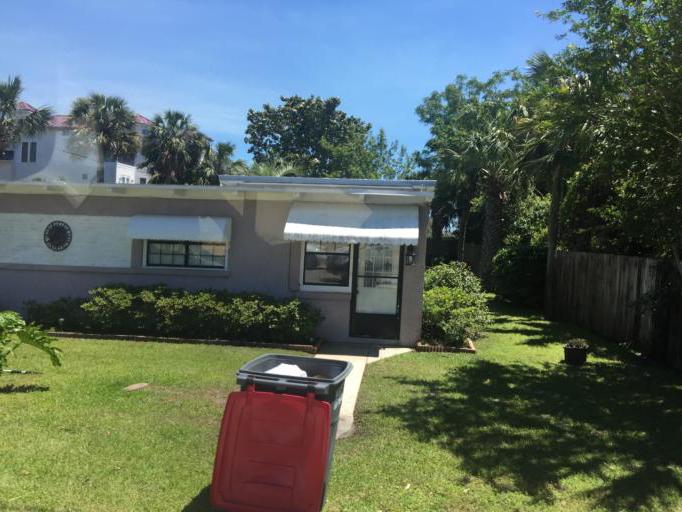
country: US
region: Florida
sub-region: Bay County
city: Laguna Beach
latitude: 30.2445
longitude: -85.9328
